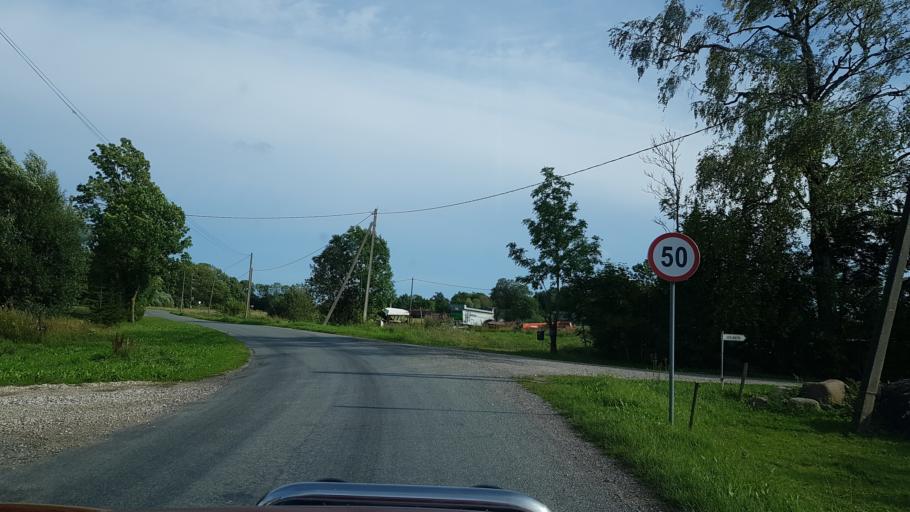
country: EE
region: Laeaene
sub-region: Lihula vald
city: Lihula
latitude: 58.4490
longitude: 23.9981
